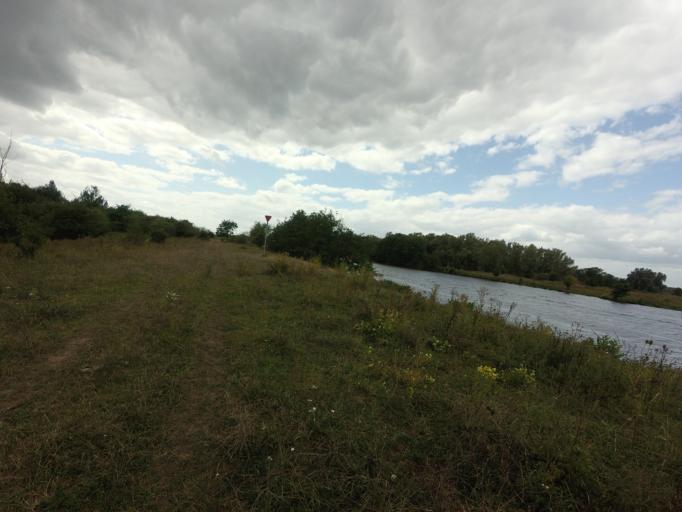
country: NL
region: Limburg
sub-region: Gemeente Maasgouw
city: Maasbracht
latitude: 51.1482
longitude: 5.8621
